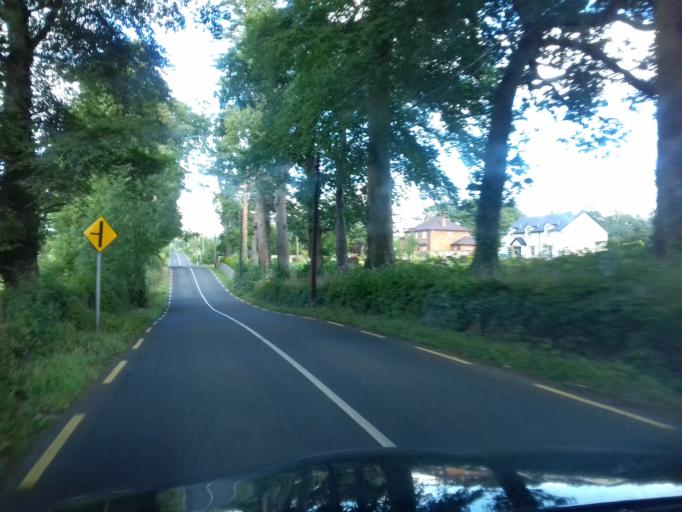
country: IE
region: Leinster
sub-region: Kilkenny
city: Thomastown
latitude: 52.5311
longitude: -7.1173
